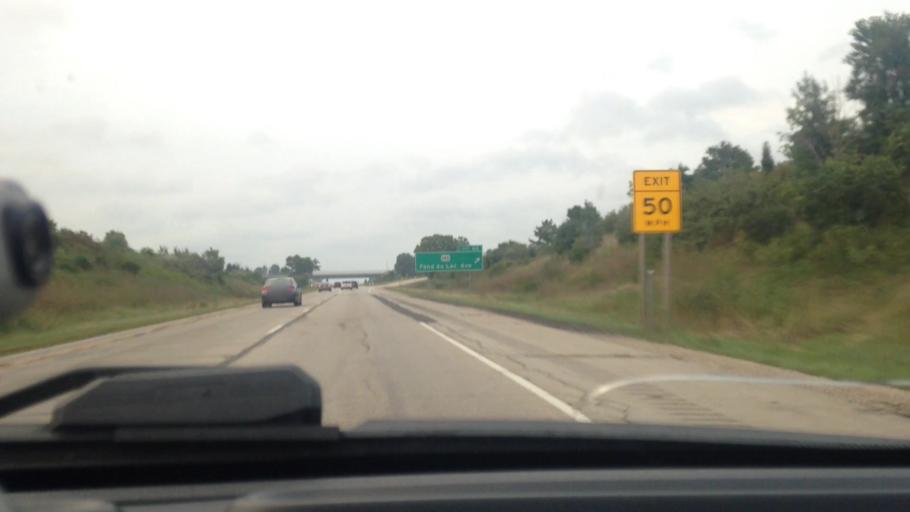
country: US
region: Wisconsin
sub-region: Washington County
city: Richfield
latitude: 43.2777
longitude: -88.1851
